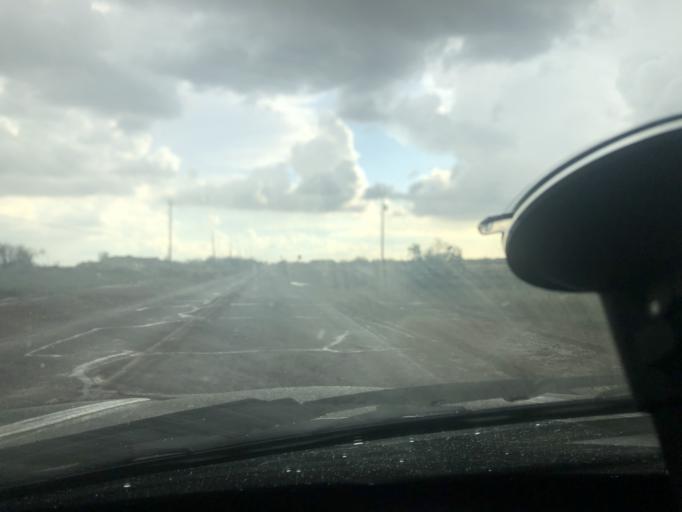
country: US
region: Arizona
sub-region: Maricopa County
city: Scottsdale
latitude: 33.4943
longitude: -111.8828
